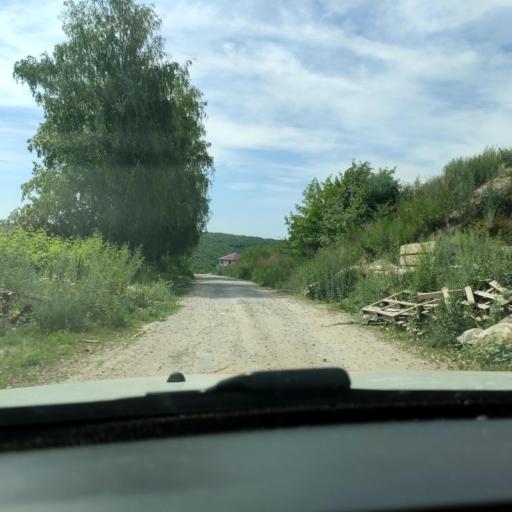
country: RU
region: Samara
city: Volzhskiy
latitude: 53.3410
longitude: 50.2000
